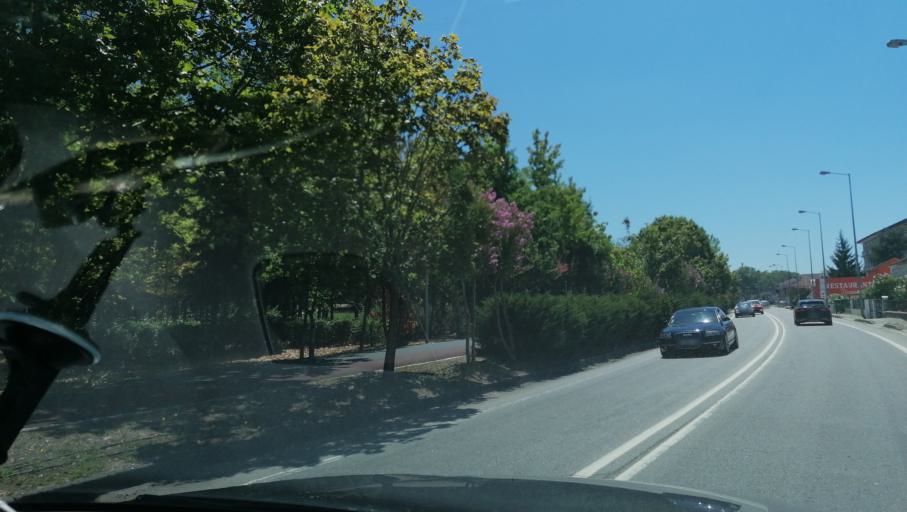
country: PT
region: Aveiro
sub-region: Mealhada
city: Mealhada
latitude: 40.3857
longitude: -8.4506
